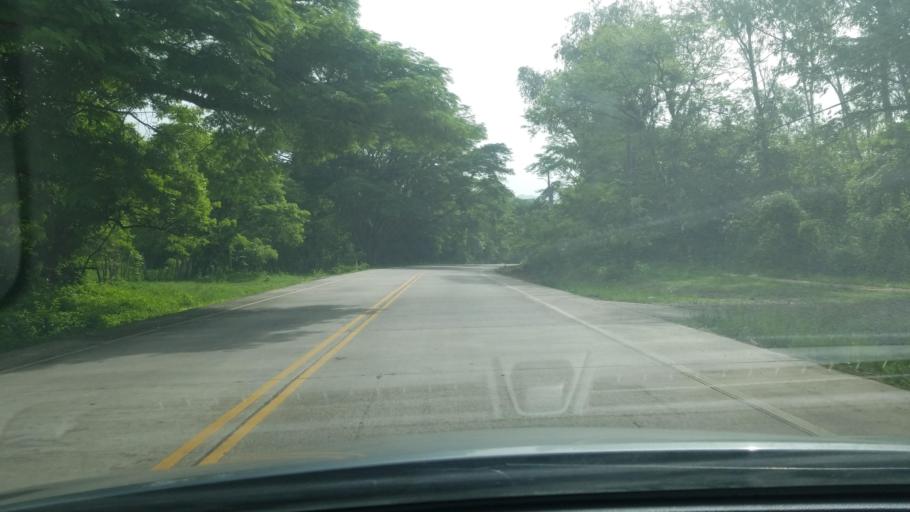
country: HN
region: Copan
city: Copan
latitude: 14.8425
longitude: -89.1424
